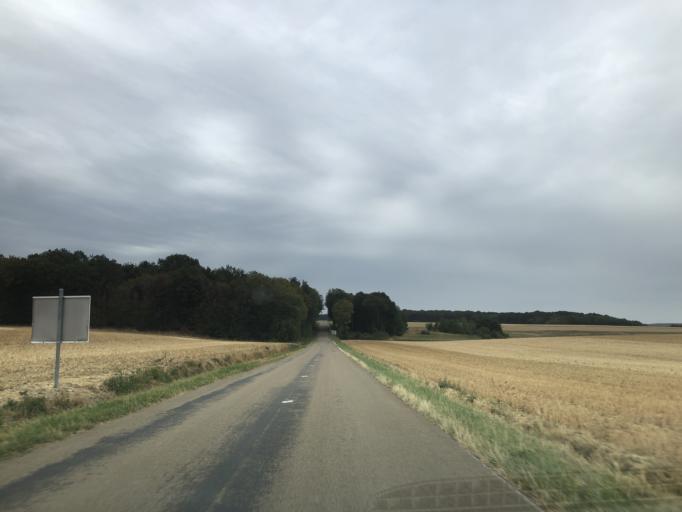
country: FR
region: Centre
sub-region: Departement du Loiret
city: Douchy
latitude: 47.9718
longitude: 3.1438
